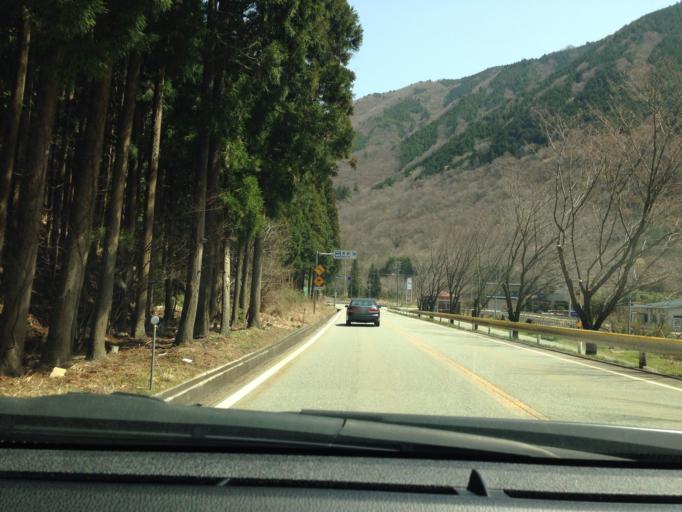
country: JP
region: Gifu
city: Takayama
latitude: 36.0028
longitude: 137.2902
